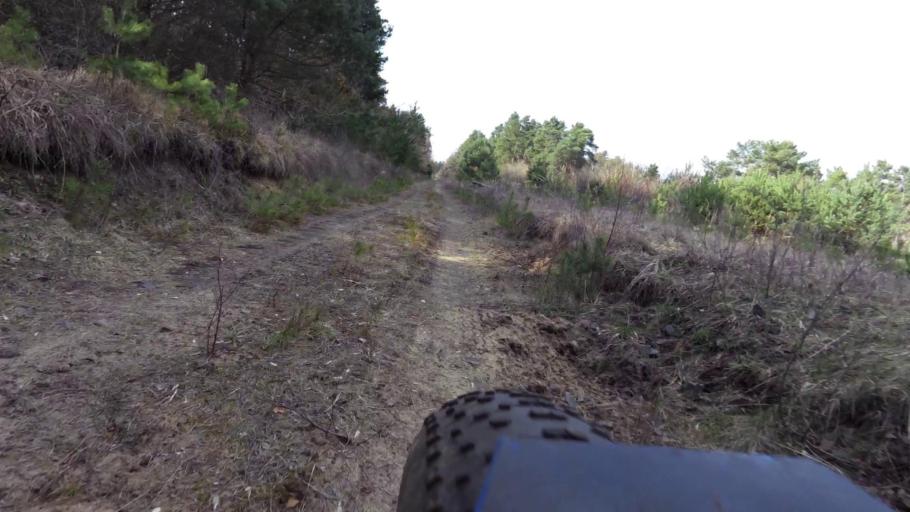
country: PL
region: Lubusz
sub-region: Powiat slubicki
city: Cybinka
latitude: 52.2374
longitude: 14.7759
